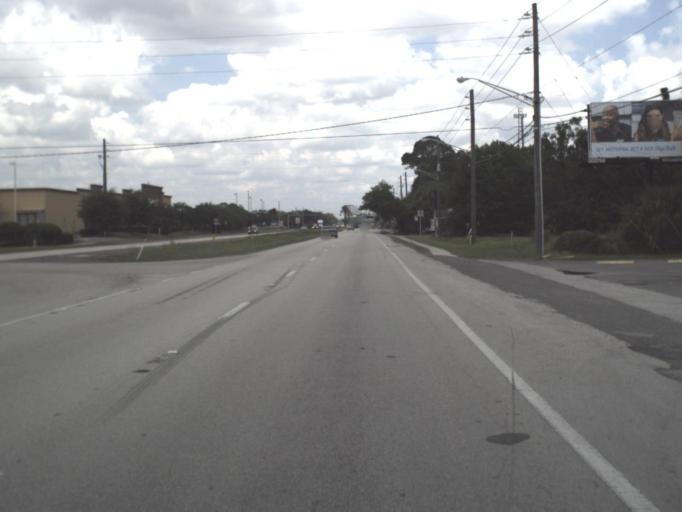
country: US
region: Florida
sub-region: Duval County
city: Jacksonville
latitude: 30.2782
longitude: -81.6267
